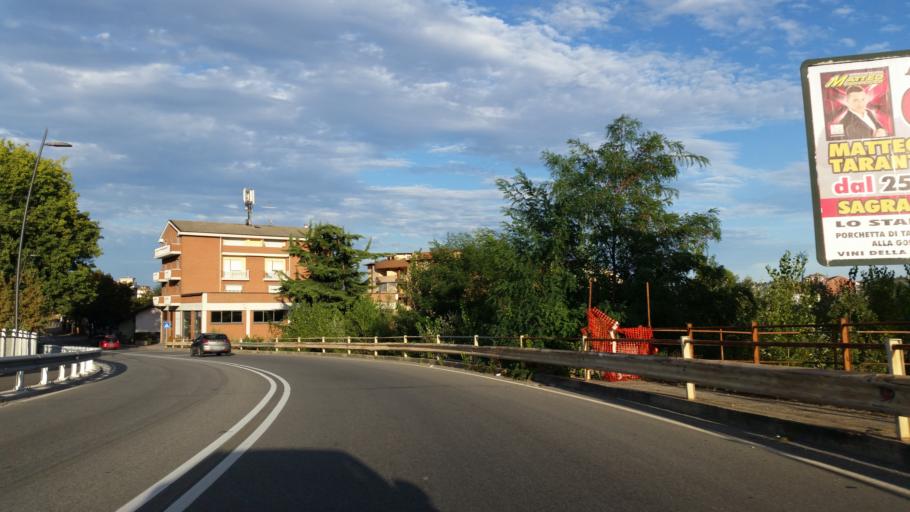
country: IT
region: Piedmont
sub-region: Provincia di Asti
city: Asti
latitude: 44.8914
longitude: 8.2020
